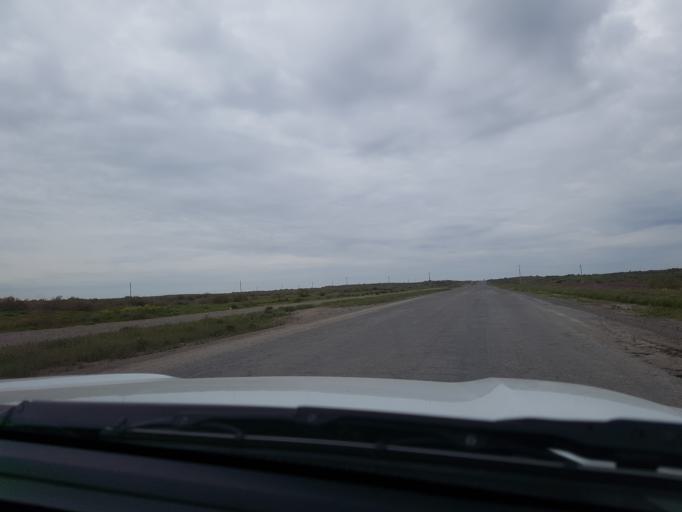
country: TM
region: Mary
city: Bayramaly
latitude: 37.9208
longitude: 62.6236
